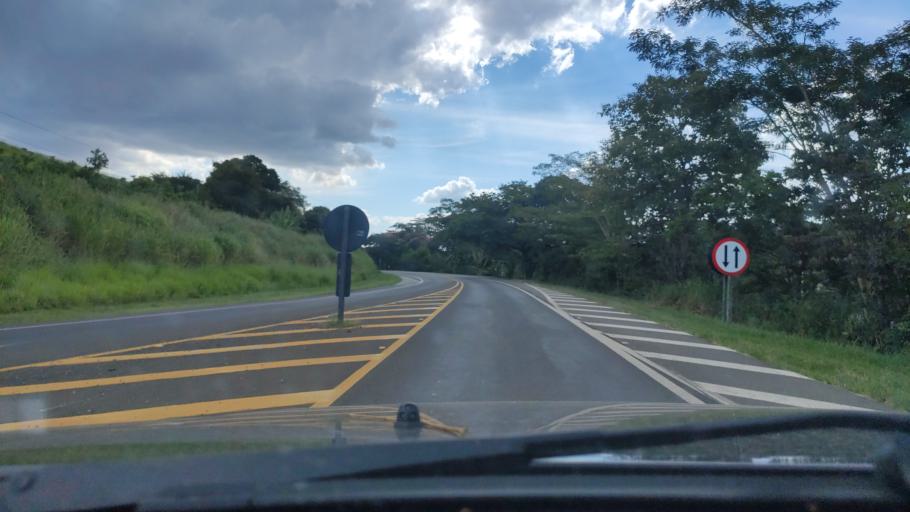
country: BR
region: Sao Paulo
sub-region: Aguas De Lindoia
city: Aguas de Lindoia
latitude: -22.4613
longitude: -46.7233
